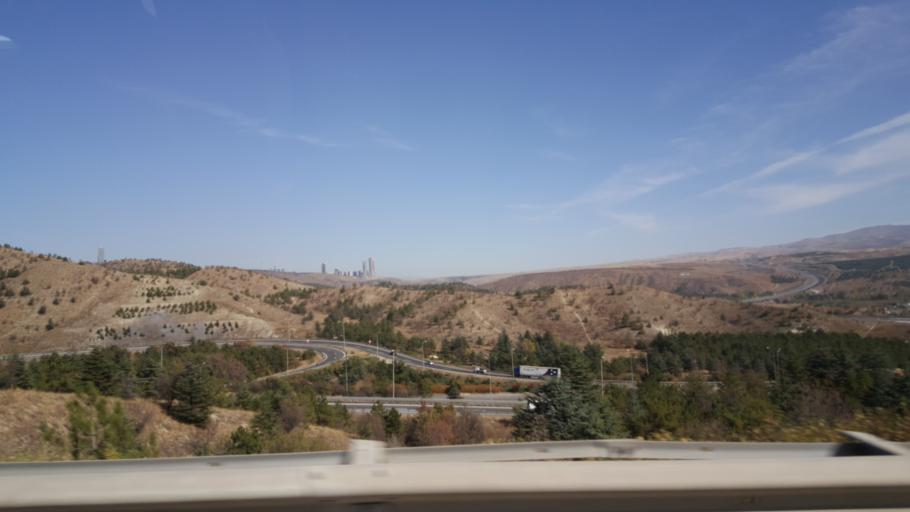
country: TR
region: Ankara
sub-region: Goelbasi
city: Golbasi
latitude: 39.8119
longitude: 32.7988
